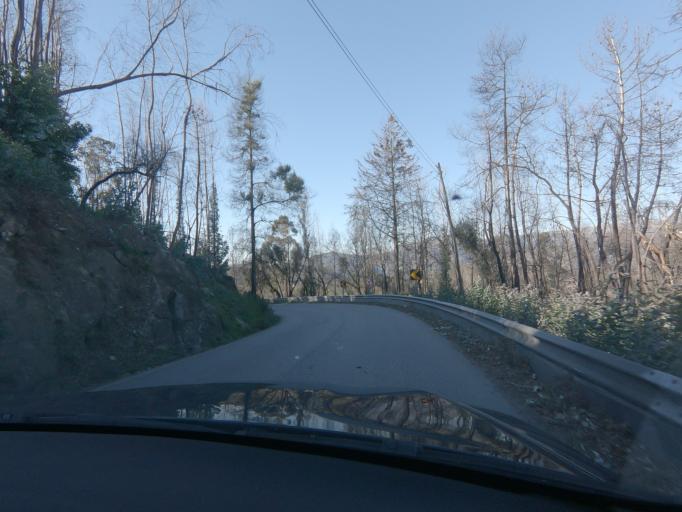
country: PT
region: Viseu
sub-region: Oliveira de Frades
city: Oliveira de Frades
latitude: 40.7319
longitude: -8.1490
